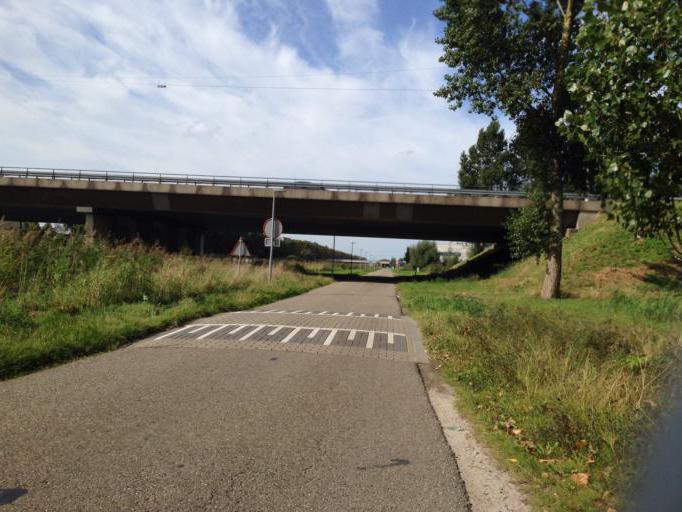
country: NL
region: Flevoland
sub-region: Gemeente Almere
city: Almere Stad
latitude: 52.3598
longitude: 5.2699
